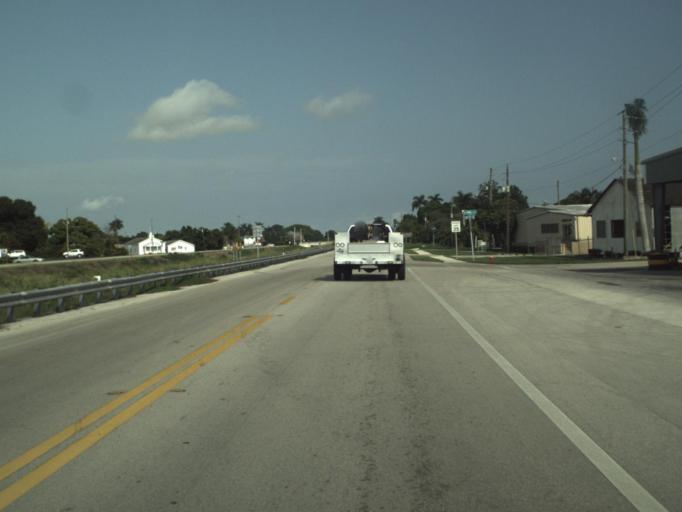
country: US
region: Florida
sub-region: Palm Beach County
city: Belle Glade
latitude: 26.6919
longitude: -80.6791
